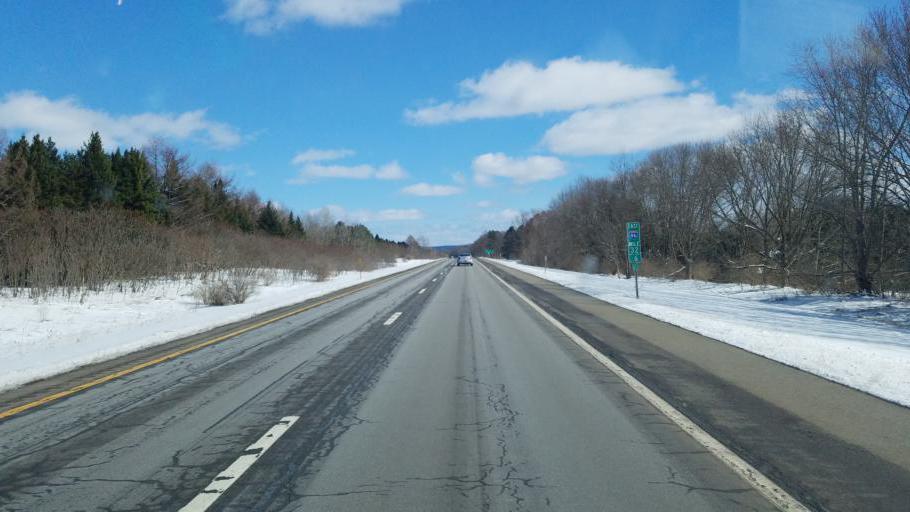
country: US
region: New York
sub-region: Chautauqua County
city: Falconer
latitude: 42.1368
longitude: -79.1589
